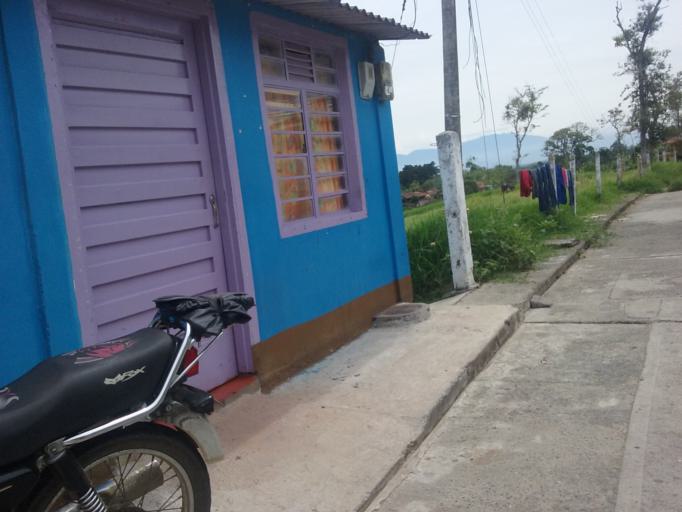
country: CO
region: Valle del Cauca
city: Ulloa
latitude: 4.7248
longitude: -75.7624
